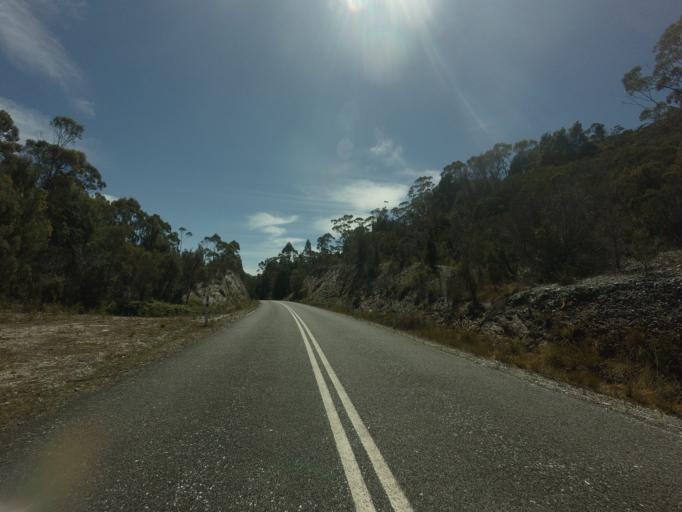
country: AU
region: Tasmania
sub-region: West Coast
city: Queenstown
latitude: -42.7742
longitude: 146.0281
